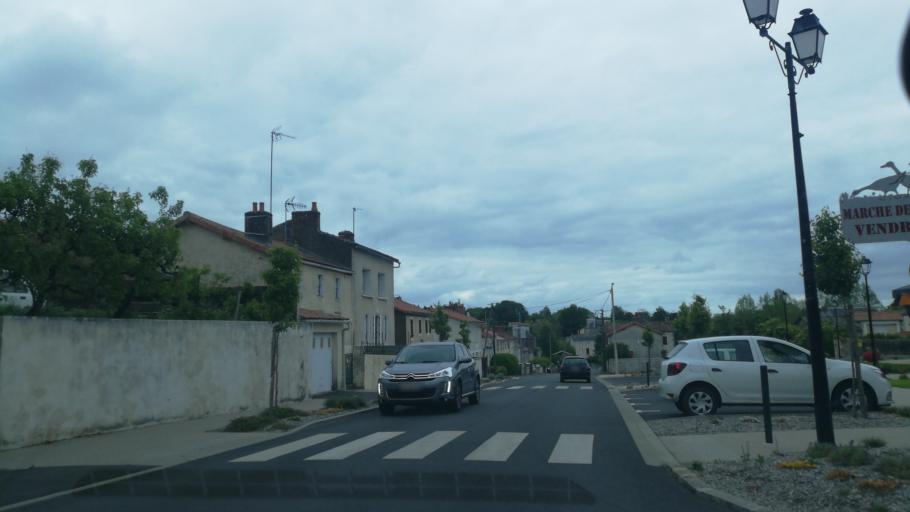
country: FR
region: Poitou-Charentes
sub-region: Departement des Deux-Sevres
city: Boisme
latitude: 46.7746
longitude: -0.4364
